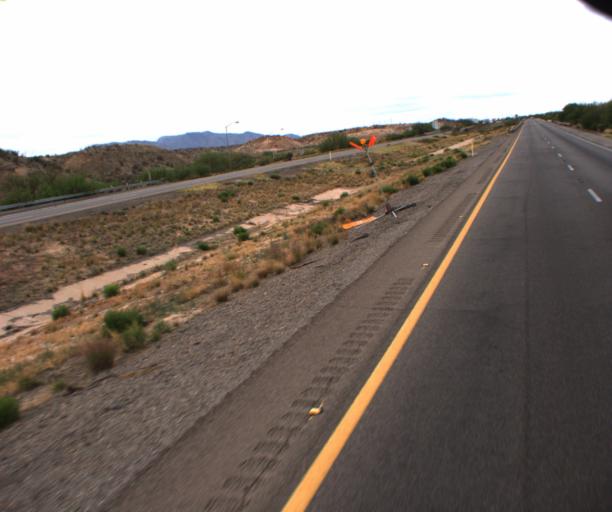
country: US
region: Arizona
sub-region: Cochise County
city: Whetstone
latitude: 31.9744
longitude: -110.3212
